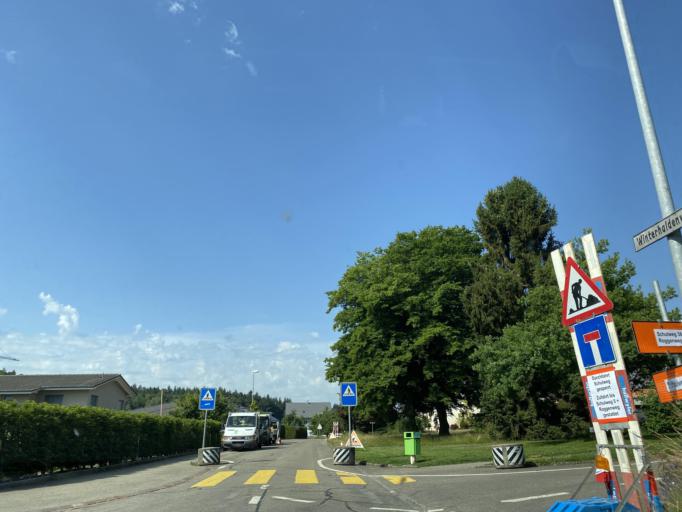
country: CH
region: Aargau
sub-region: Bezirk Zofingen
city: Rothrist
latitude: 47.3008
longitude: 7.8819
